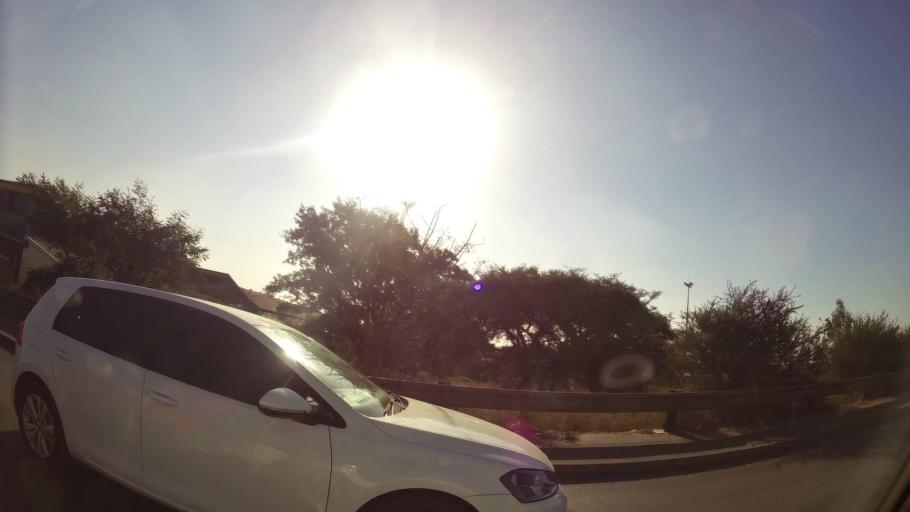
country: ZA
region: North-West
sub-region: Bojanala Platinum District Municipality
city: Rustenburg
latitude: -25.6704
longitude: 27.2549
